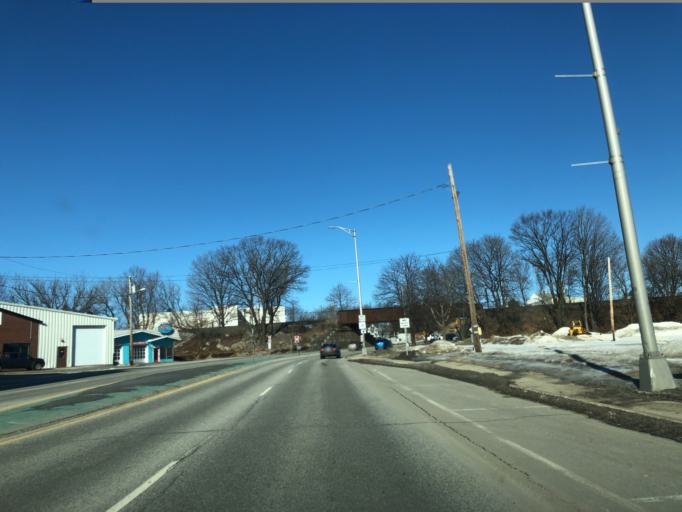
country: US
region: Maine
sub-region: Androscoggin County
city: Auburn
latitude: 44.0994
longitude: -70.2267
